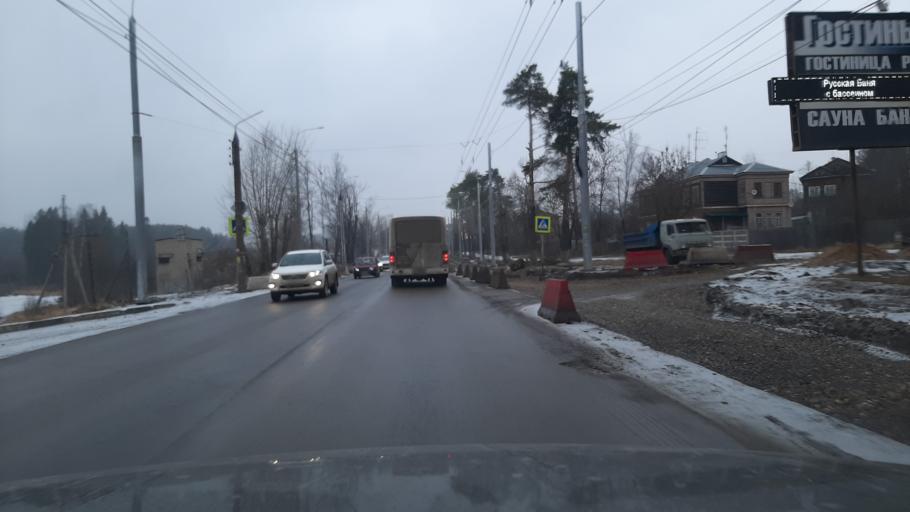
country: RU
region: Ivanovo
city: Kokhma
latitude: 56.9361
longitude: 41.0697
